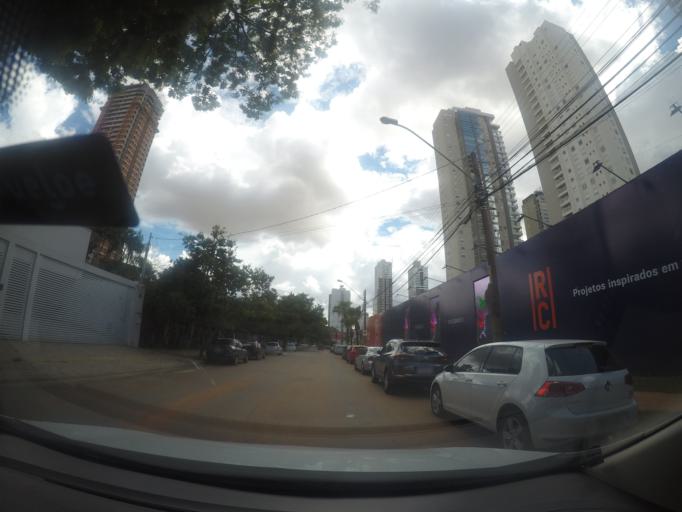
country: BR
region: Goias
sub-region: Goiania
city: Goiania
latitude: -16.7028
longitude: -49.2673
